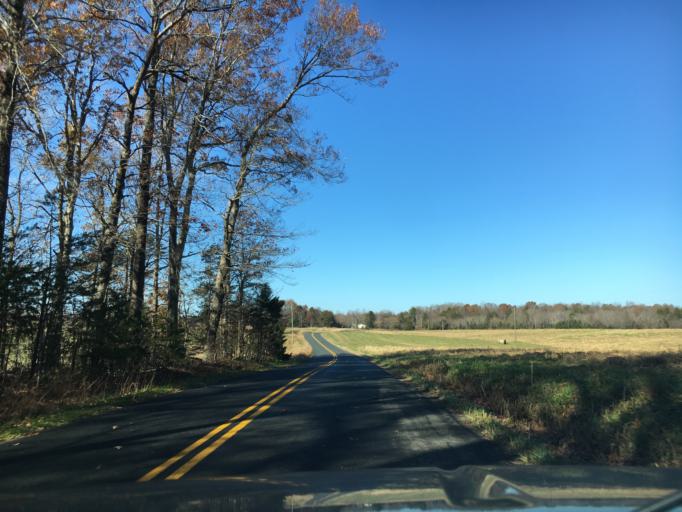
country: US
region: Virginia
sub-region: Buckingham County
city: Buckingham
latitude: 37.4230
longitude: -78.6110
